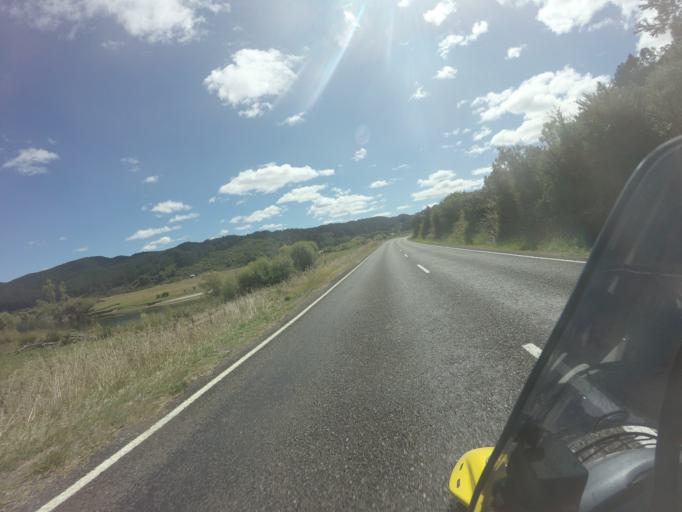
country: NZ
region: Bay of Plenty
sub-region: Kawerau District
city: Kawerau
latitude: -38.1879
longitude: 176.8381
